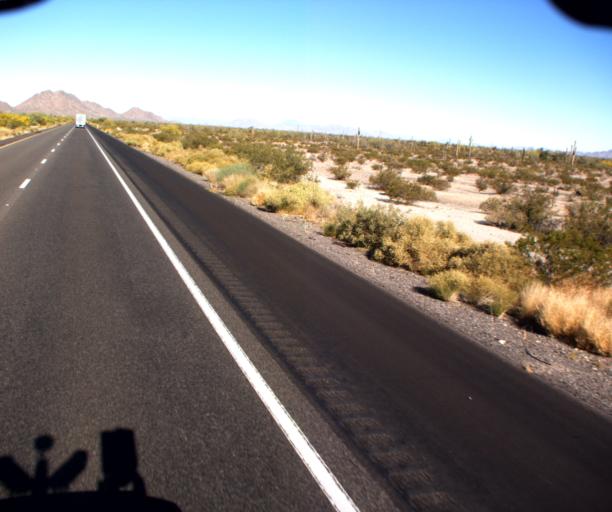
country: US
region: Arizona
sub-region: Maricopa County
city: Gila Bend
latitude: 32.8967
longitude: -112.5023
